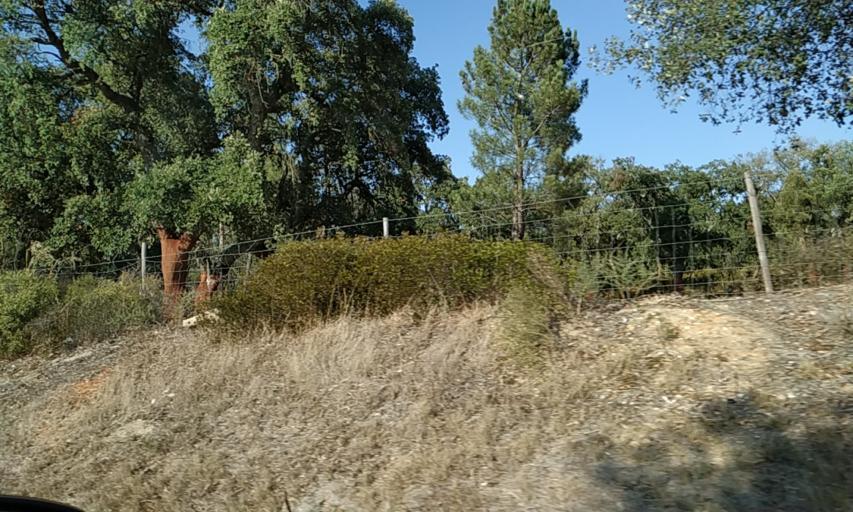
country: PT
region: Santarem
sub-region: Almeirim
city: Fazendas de Almeirim
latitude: 39.1403
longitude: -8.6124
